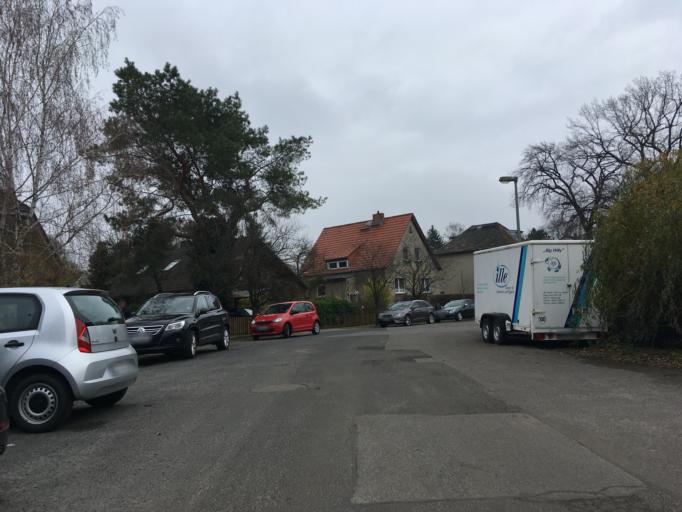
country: DE
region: Berlin
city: Wilhelmsruh
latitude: 52.5849
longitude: 13.3780
